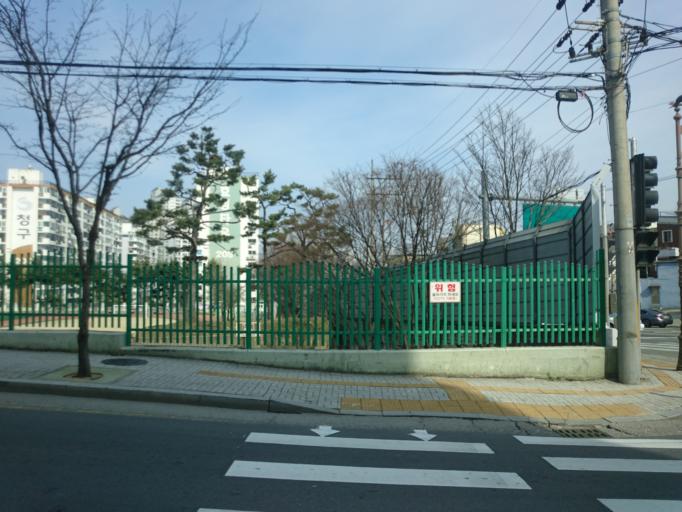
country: KR
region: Daegu
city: Daegu
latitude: 35.8338
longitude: 128.6006
